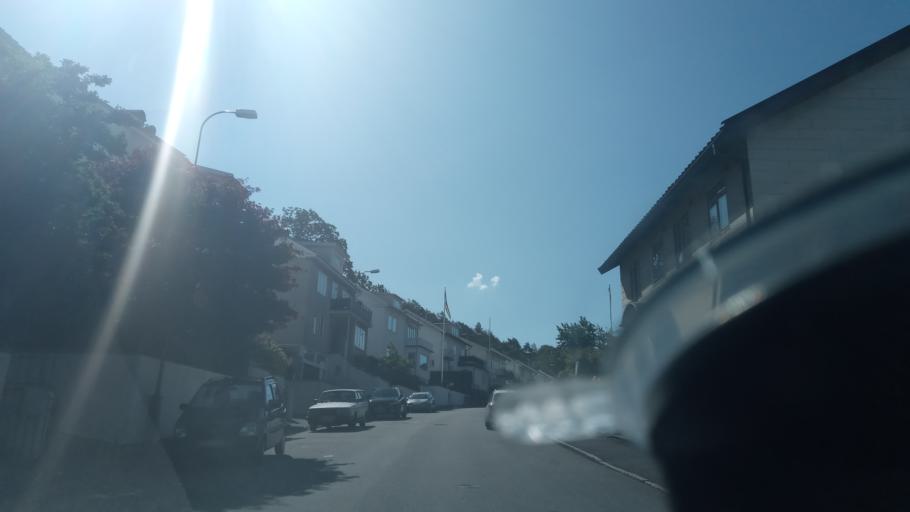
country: SE
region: Vaestra Goetaland
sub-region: Molndal
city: Moelndal
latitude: 57.6945
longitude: 12.0110
